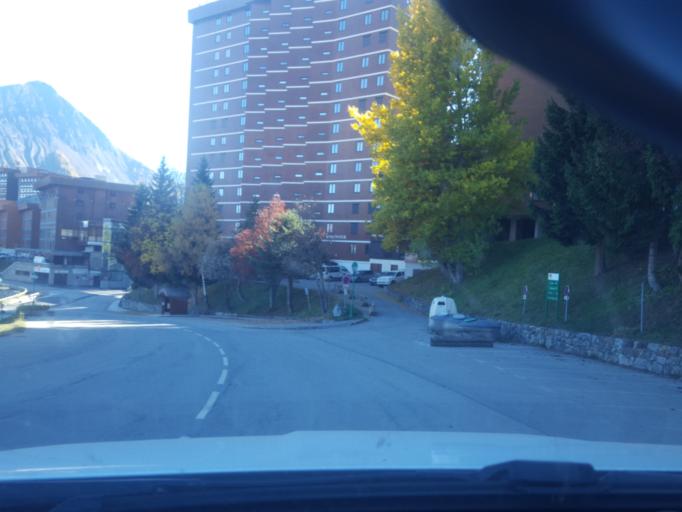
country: FR
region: Rhone-Alpes
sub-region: Departement de la Savoie
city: Saint-Jean-de-Maurienne
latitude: 45.2422
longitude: 6.2673
